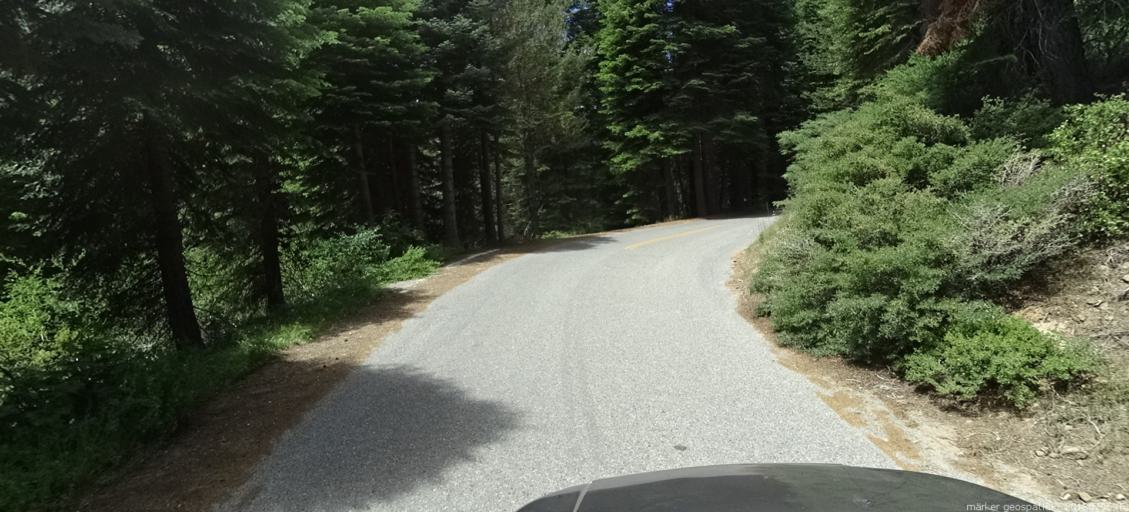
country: US
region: California
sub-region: Madera County
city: Oakhurst
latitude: 37.4334
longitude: -119.4325
